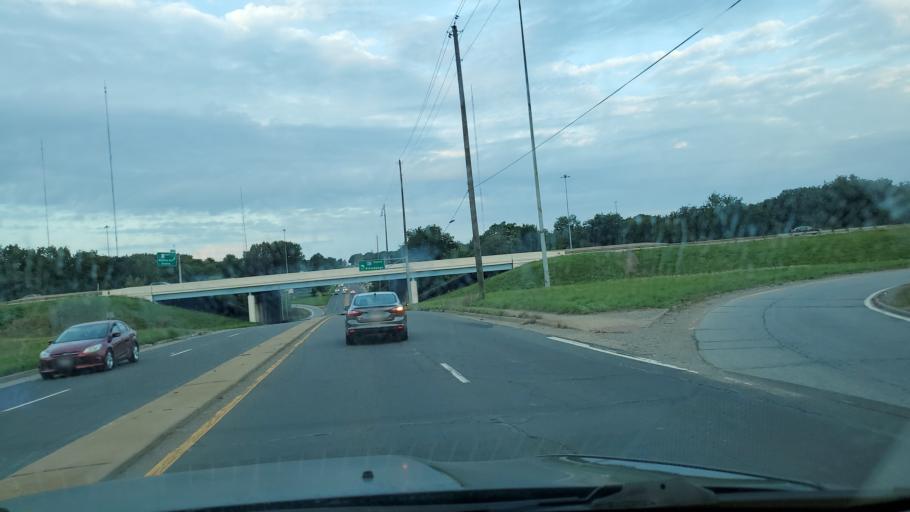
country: US
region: Ohio
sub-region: Mahoning County
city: Struthers
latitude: 41.0607
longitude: -80.6265
